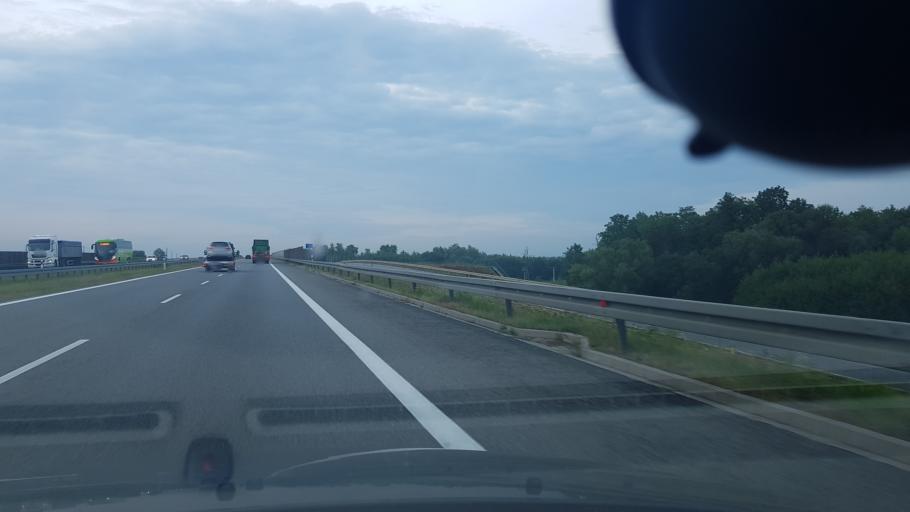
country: PL
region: Warmian-Masurian Voivodeship
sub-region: Powiat elblaski
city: Paslek
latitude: 54.0259
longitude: 19.6754
